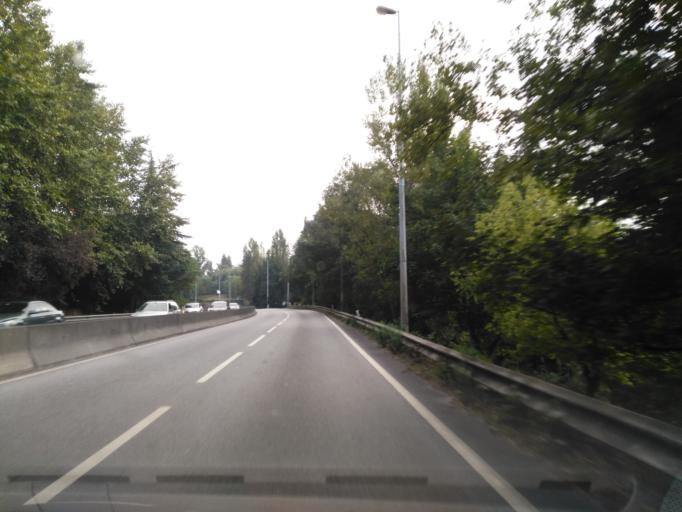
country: PT
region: Braga
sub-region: Guimaraes
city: Guimaraes
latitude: 41.4460
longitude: -8.3083
